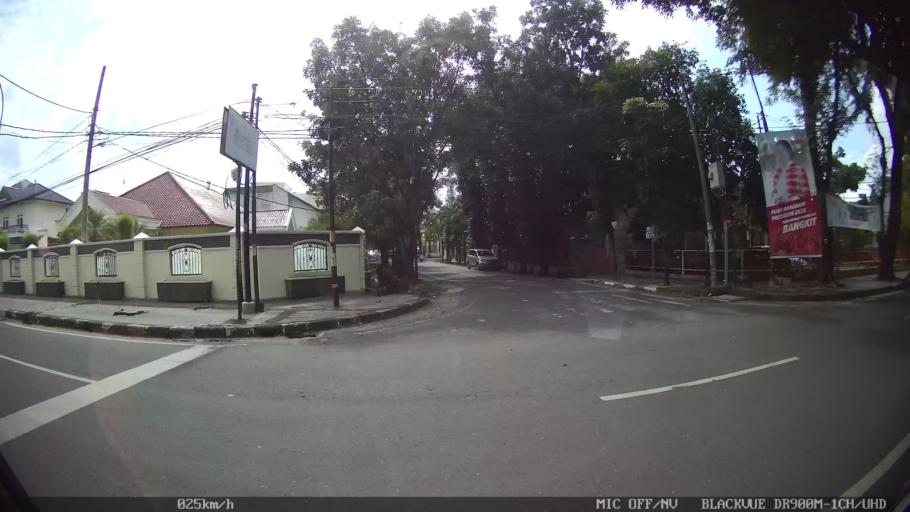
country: ID
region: North Sumatra
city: Medan
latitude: 3.5800
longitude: 98.6672
